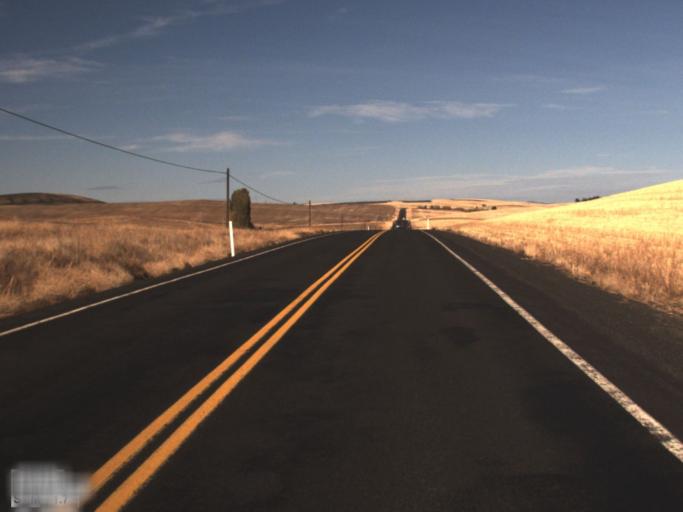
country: US
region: Washington
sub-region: Lincoln County
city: Davenport
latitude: 47.6802
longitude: -118.1410
